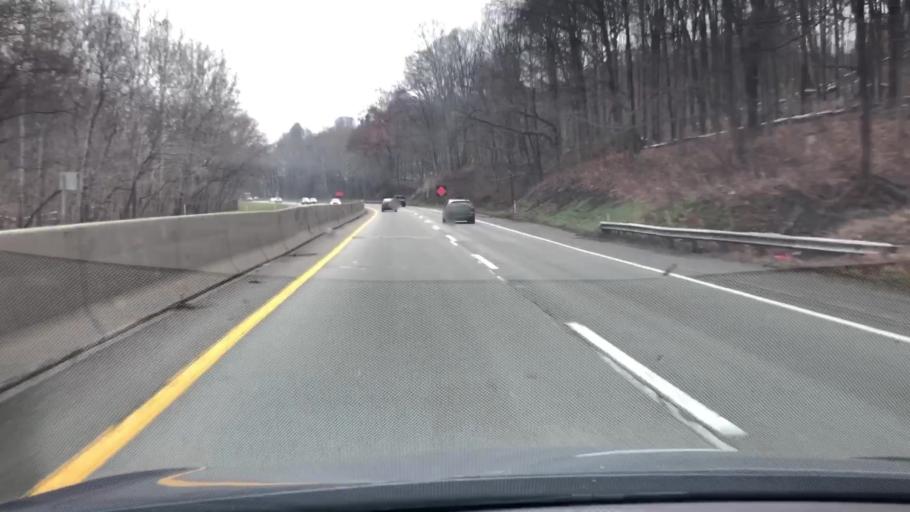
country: US
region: Pennsylvania
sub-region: Westmoreland County
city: Level Green
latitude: 40.4063
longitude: -79.7187
